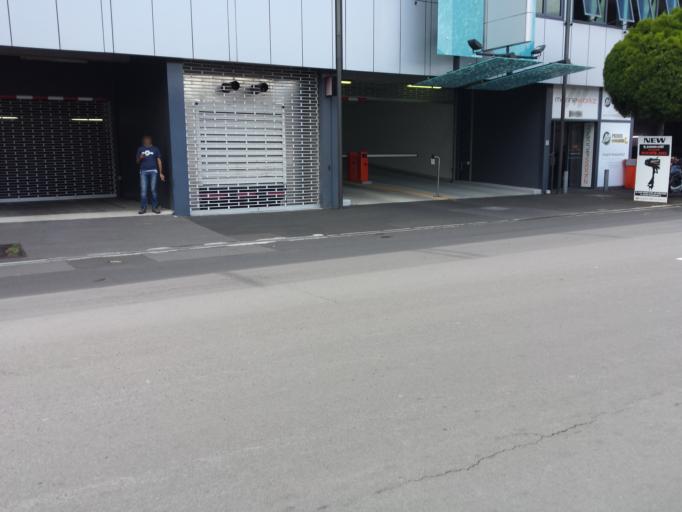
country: NZ
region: Auckland
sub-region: Auckland
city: Auckland
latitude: -36.8441
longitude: 174.7526
